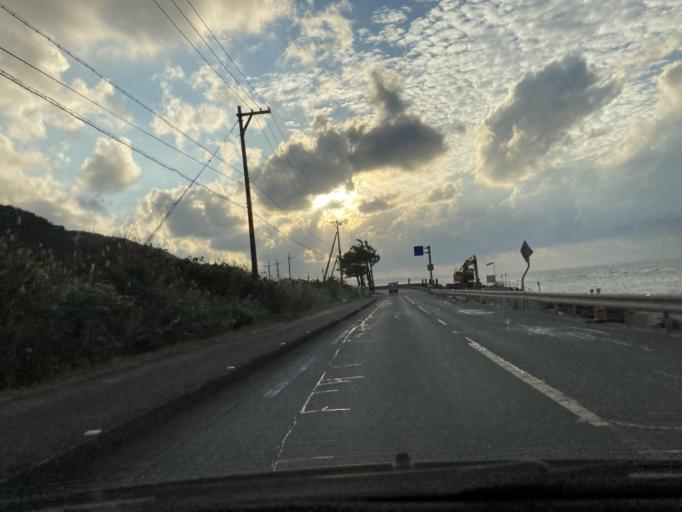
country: JP
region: Okinawa
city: Nago
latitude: 26.7823
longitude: 128.2159
